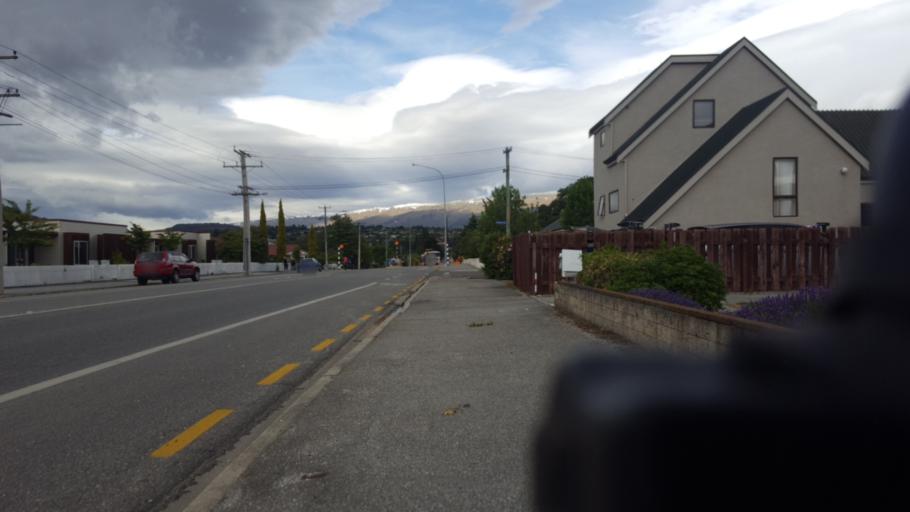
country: NZ
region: Otago
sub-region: Queenstown-Lakes District
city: Wanaka
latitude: -45.2493
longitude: 169.3979
